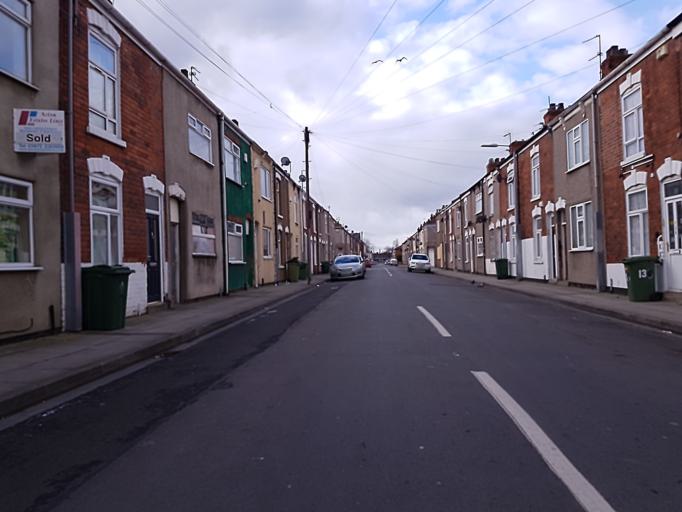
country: GB
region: England
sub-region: North East Lincolnshire
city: Grimsby
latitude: 53.5689
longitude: -0.0615
